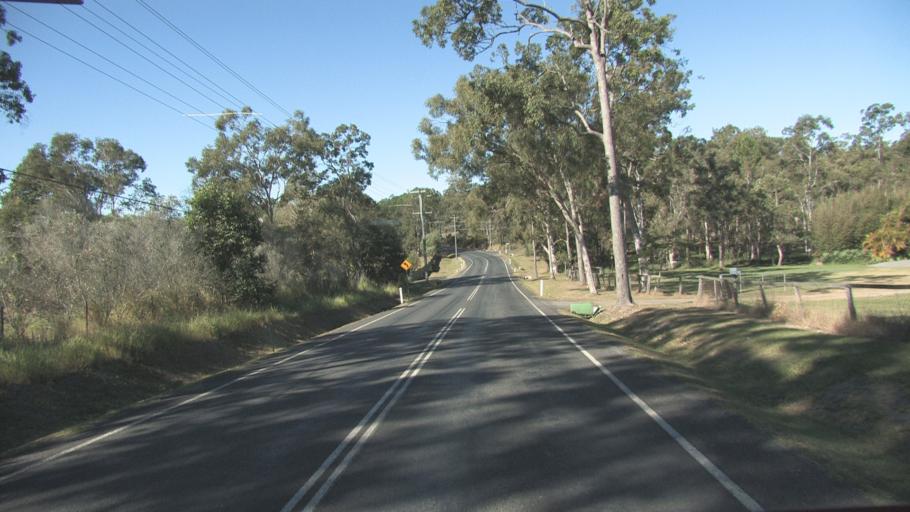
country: AU
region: Queensland
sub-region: Logan
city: Park Ridge South
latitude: -27.7240
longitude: 153.0109
